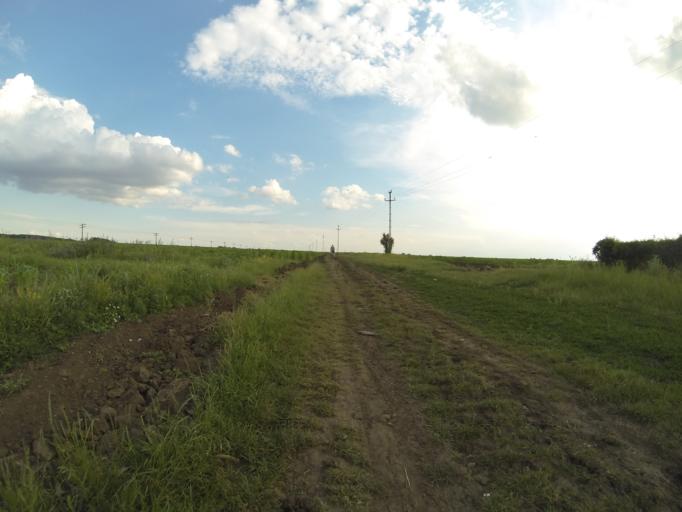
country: RO
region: Dolj
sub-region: Comuna Caloparu
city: Salcuta
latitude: 44.1558
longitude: 23.7055
